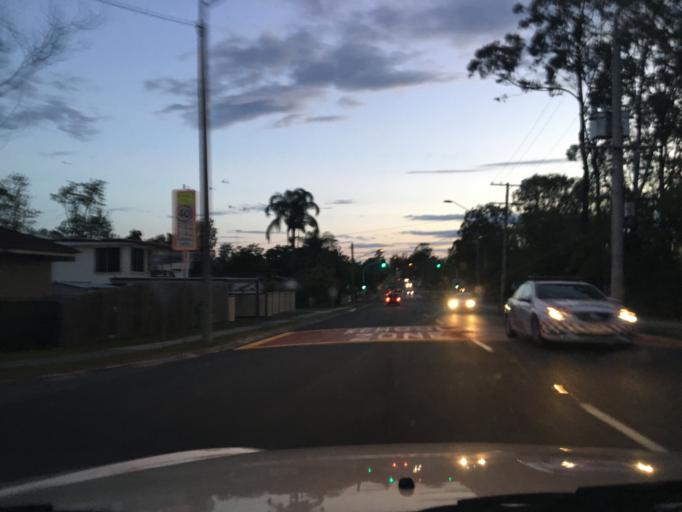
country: AU
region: Queensland
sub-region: Logan
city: Logan City
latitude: -27.6516
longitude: 153.0986
